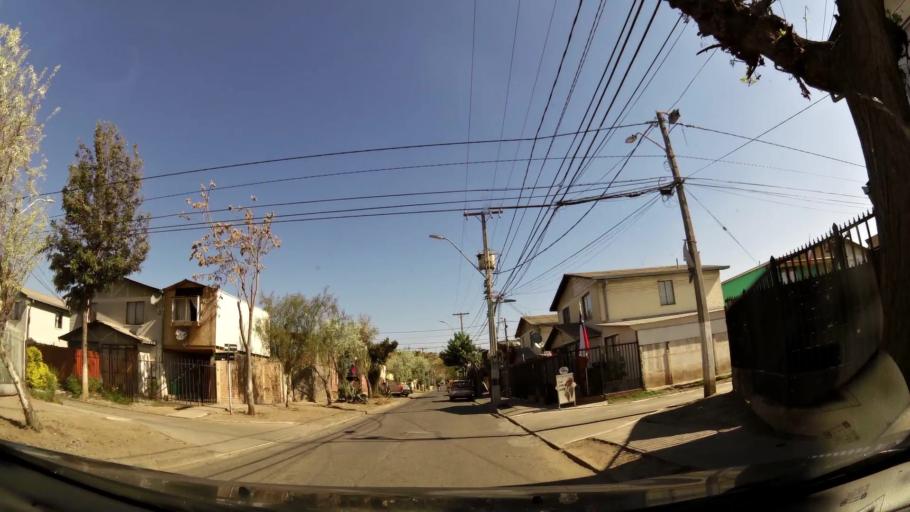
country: CL
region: Santiago Metropolitan
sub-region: Provincia de Maipo
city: San Bernardo
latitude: -33.6168
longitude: -70.7056
